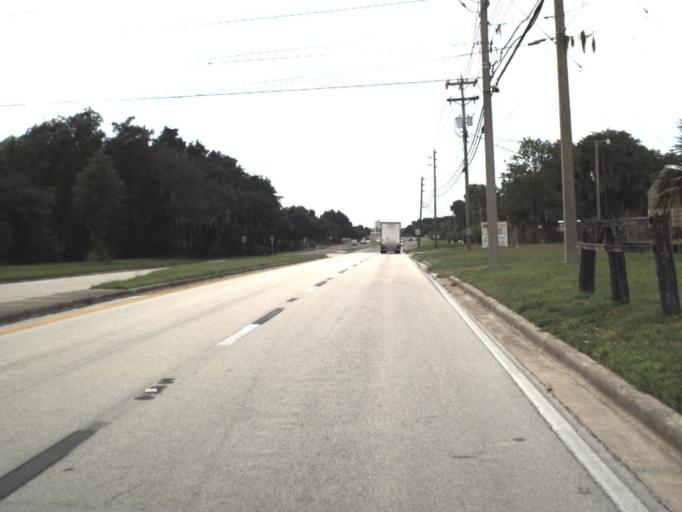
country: US
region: Florida
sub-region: Polk County
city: Bartow
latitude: 27.8700
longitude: -81.8287
